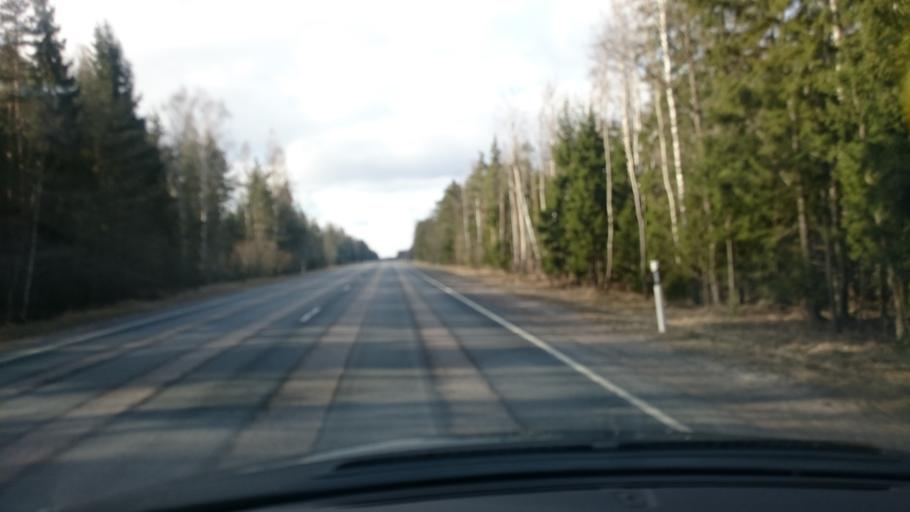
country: EE
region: Harju
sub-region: Nissi vald
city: Turba
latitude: 58.9558
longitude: 24.0780
